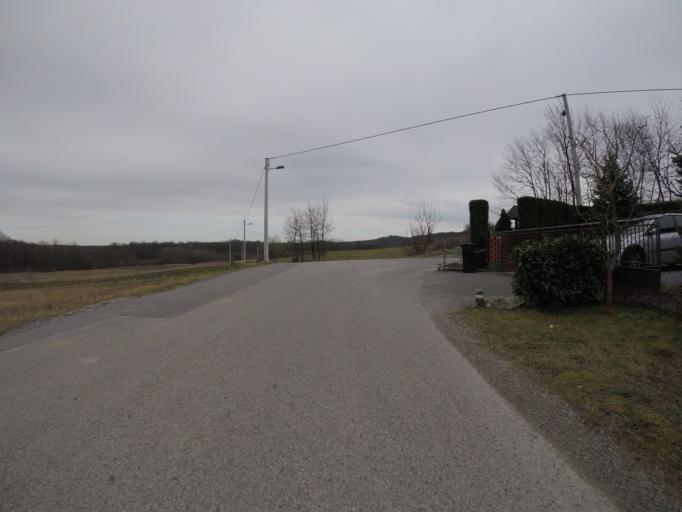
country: HR
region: Grad Zagreb
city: Strmec
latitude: 45.6693
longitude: 15.8949
